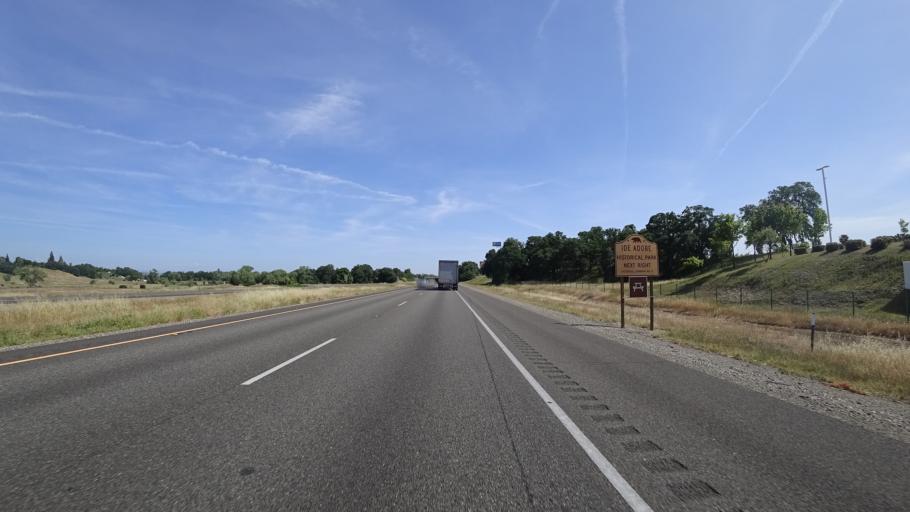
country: US
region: California
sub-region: Tehama County
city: Red Bluff
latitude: 40.1975
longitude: -122.2396
